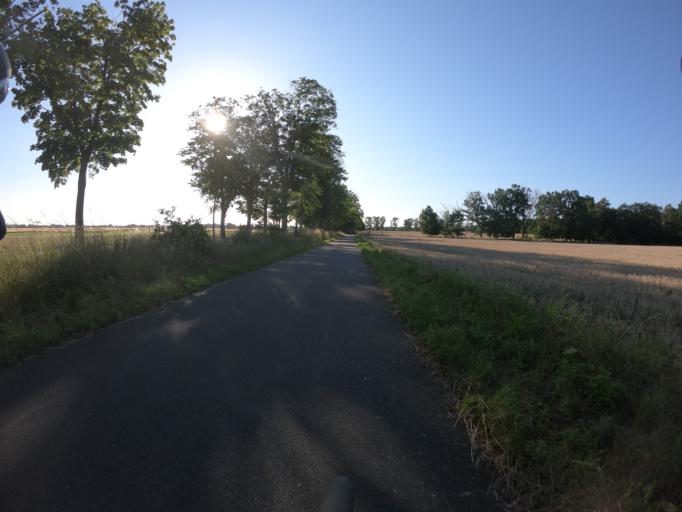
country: DE
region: Brandenburg
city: Niedergorsdorf
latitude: 51.9751
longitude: 12.9987
